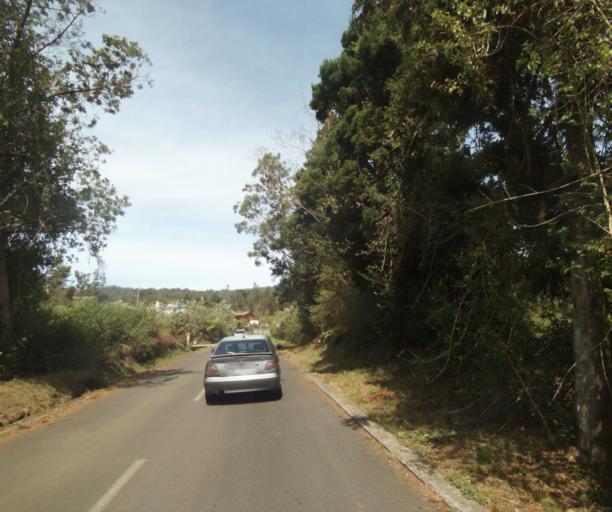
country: RE
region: Reunion
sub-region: Reunion
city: Trois-Bassins
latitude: -21.0461
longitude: 55.3319
